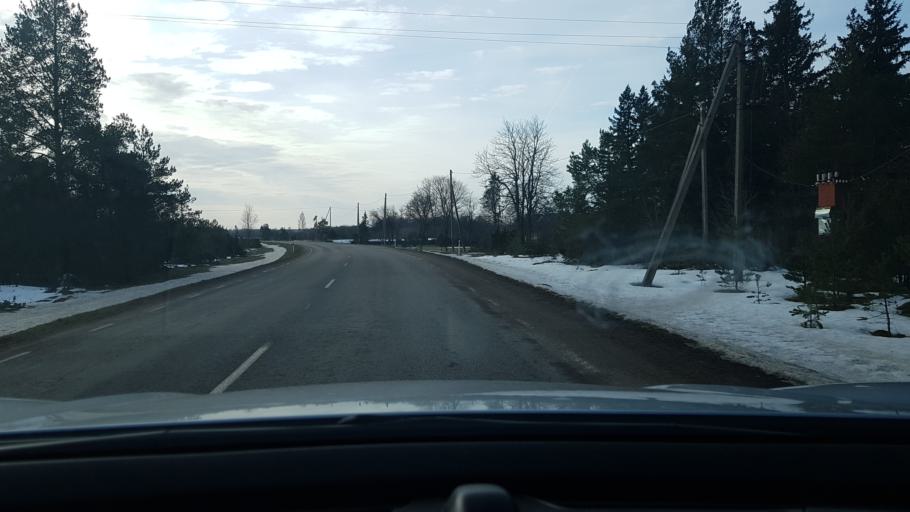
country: EE
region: Saare
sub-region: Kuressaare linn
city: Kuressaare
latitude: 58.3195
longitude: 22.5475
